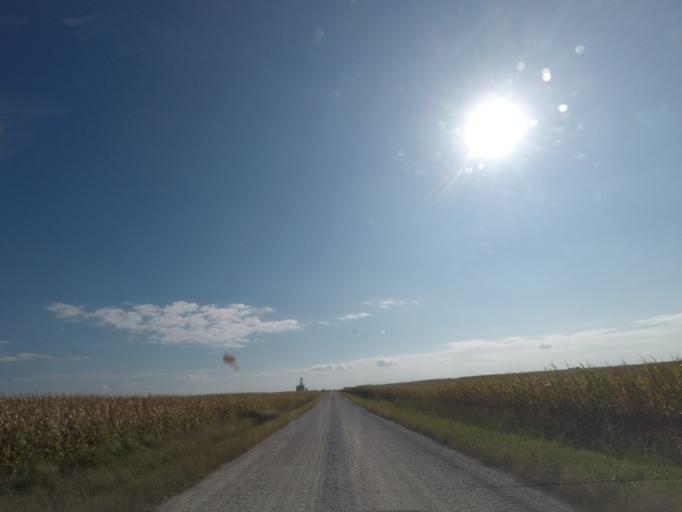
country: US
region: Iowa
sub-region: Story County
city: Nevada
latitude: 42.0490
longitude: -93.4236
